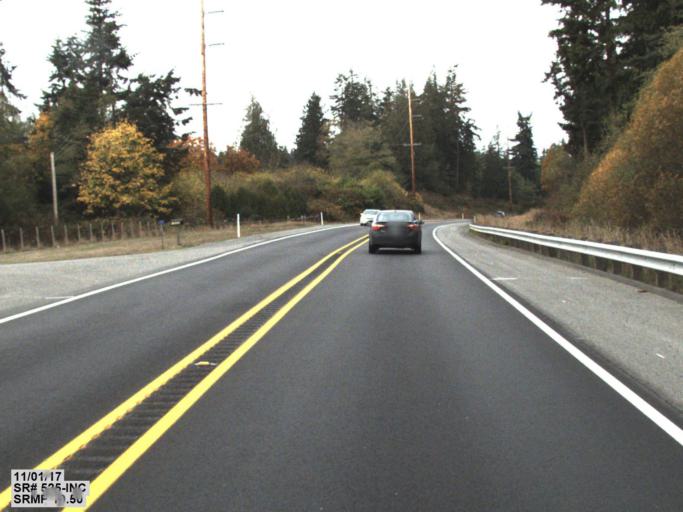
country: US
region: Washington
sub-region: Island County
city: Freeland
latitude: 48.0205
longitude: -122.5548
